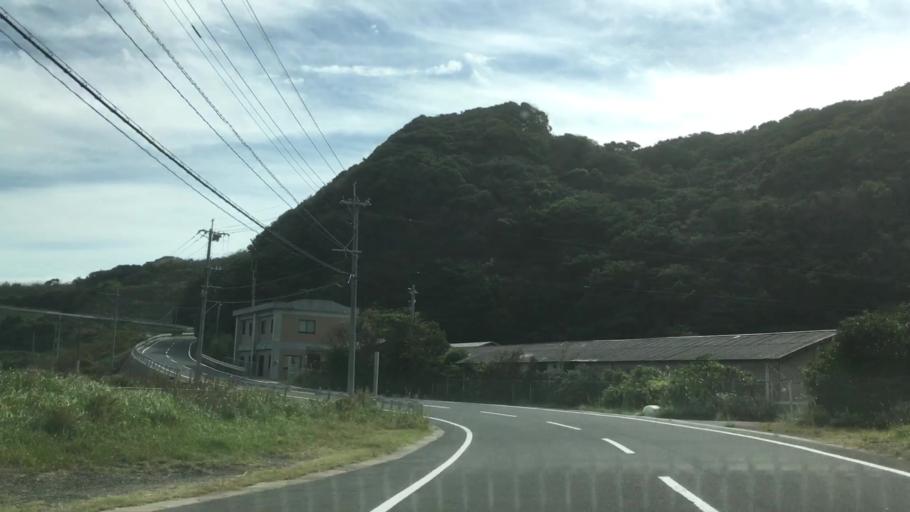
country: JP
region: Nagasaki
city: Sasebo
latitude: 33.0079
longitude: 129.5621
